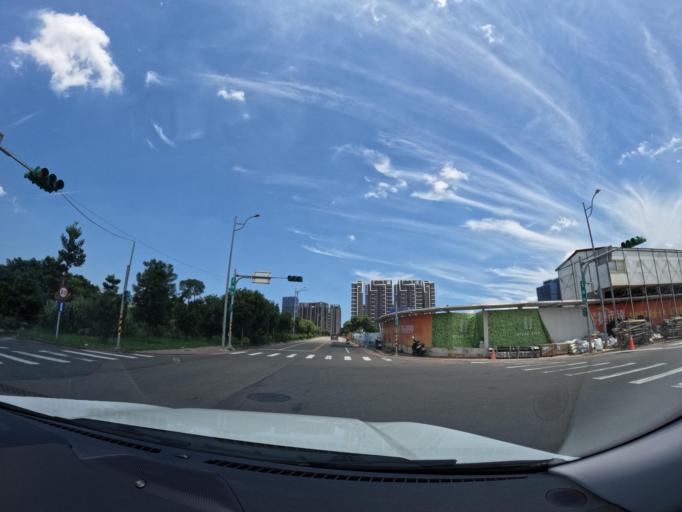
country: TW
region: Taiwan
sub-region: Taoyuan
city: Taoyuan
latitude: 25.0421
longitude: 121.3837
